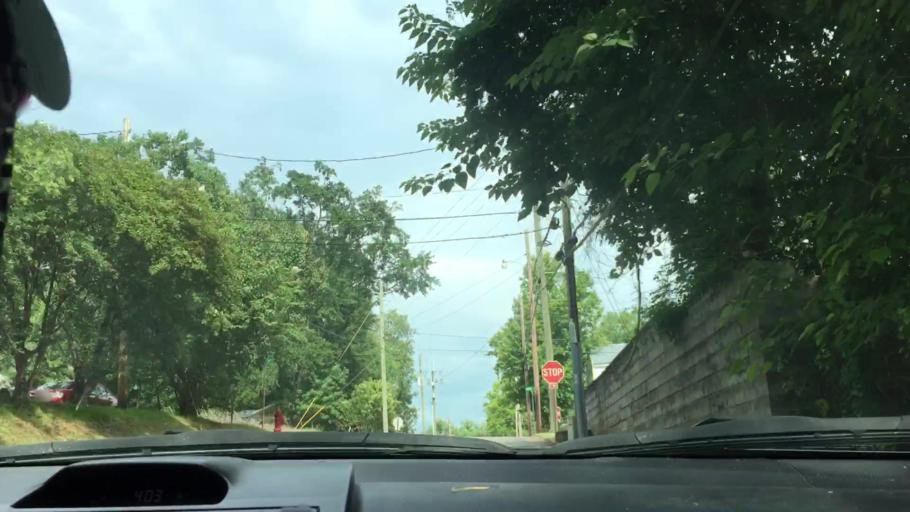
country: US
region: Alabama
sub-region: Hale County
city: Greensboro
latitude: 32.7053
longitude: -87.5941
